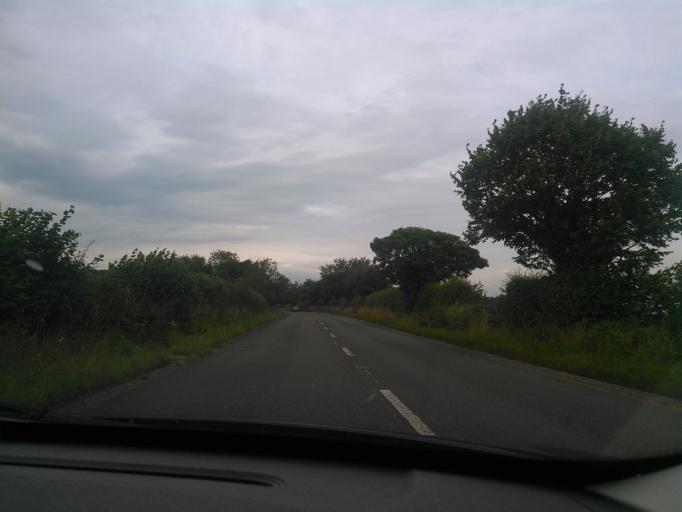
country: GB
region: England
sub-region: Shropshire
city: Stoke upon Tern
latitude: 52.8309
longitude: -2.5988
